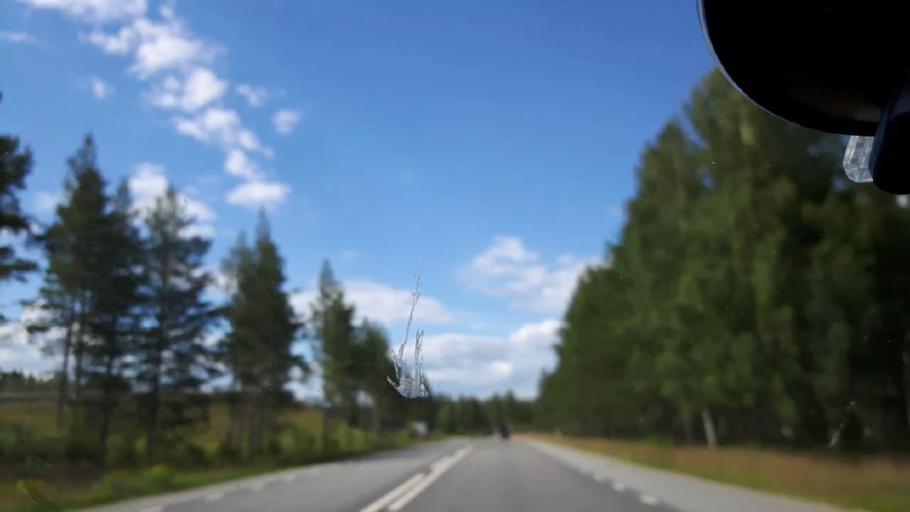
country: SE
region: Jaemtland
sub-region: Braecke Kommun
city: Braecke
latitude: 62.7588
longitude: 15.4118
